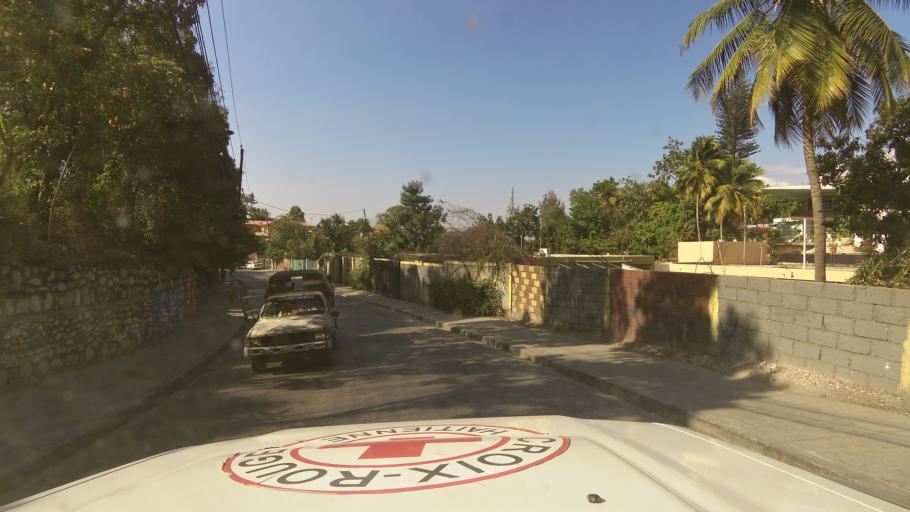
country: HT
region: Ouest
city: Petionville
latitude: 18.5147
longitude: -72.2754
